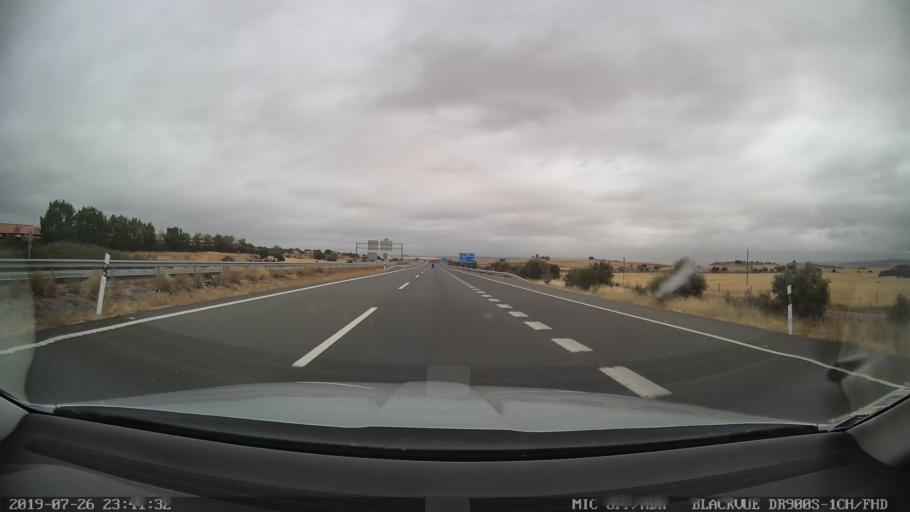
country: ES
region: Extremadura
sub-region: Provincia de Caceres
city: Trujillo
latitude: 39.4867
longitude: -5.8463
